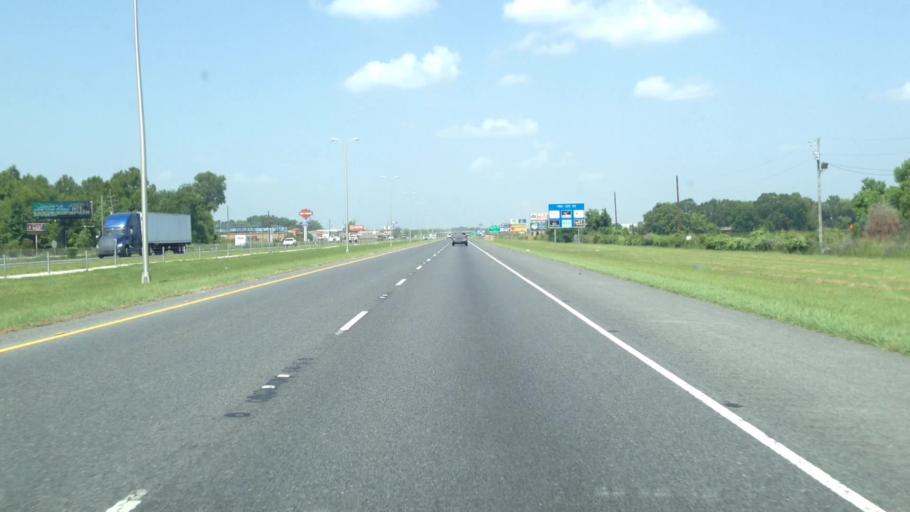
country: US
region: Louisiana
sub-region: Ouachita Parish
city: Lakeshore
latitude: 32.4931
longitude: -92.0373
